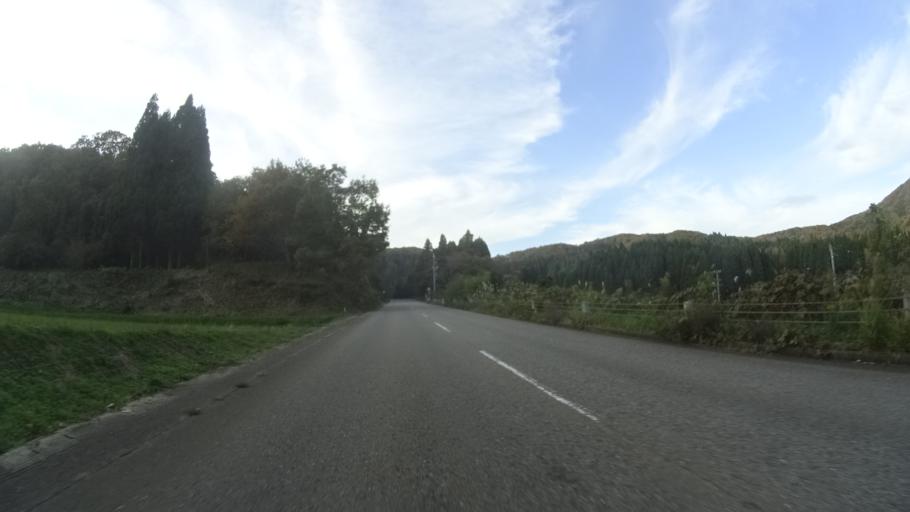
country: JP
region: Ishikawa
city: Nanao
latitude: 37.1974
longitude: 136.7134
